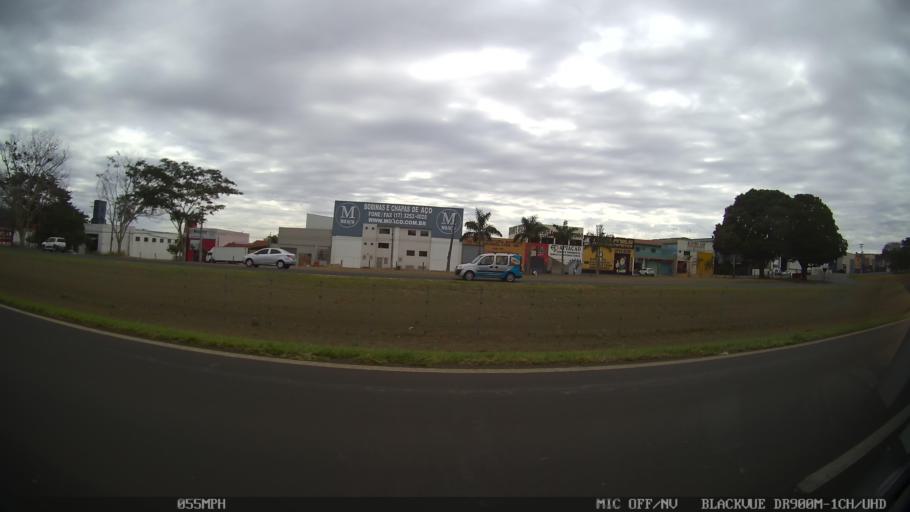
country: BR
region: Sao Paulo
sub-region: Bady Bassitt
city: Bady Bassitt
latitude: -20.8077
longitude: -49.5089
